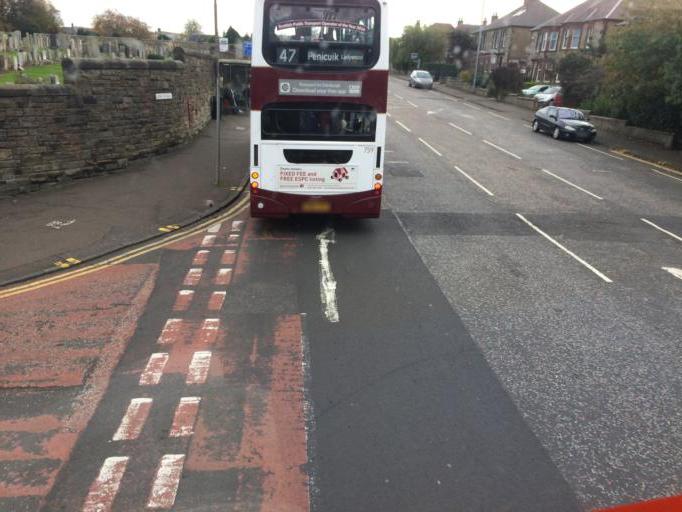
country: GB
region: Scotland
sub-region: Midlothian
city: Loanhead
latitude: 55.9146
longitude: -3.1650
